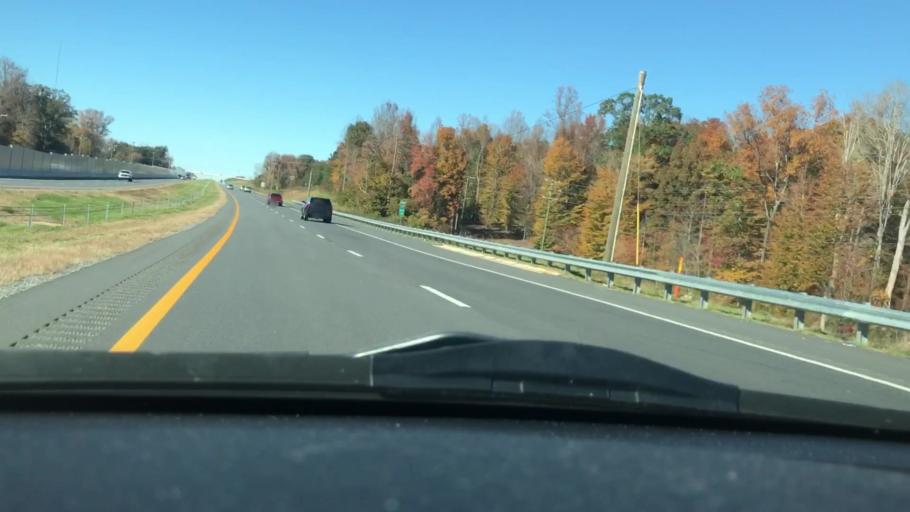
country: US
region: North Carolina
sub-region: Guilford County
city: Summerfield
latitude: 36.2559
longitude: -79.9239
